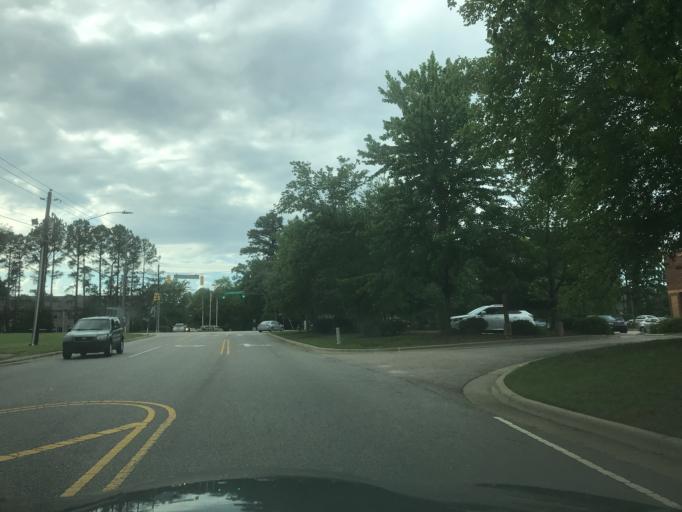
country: US
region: North Carolina
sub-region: Wake County
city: Raleigh
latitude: 35.8649
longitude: -78.5913
